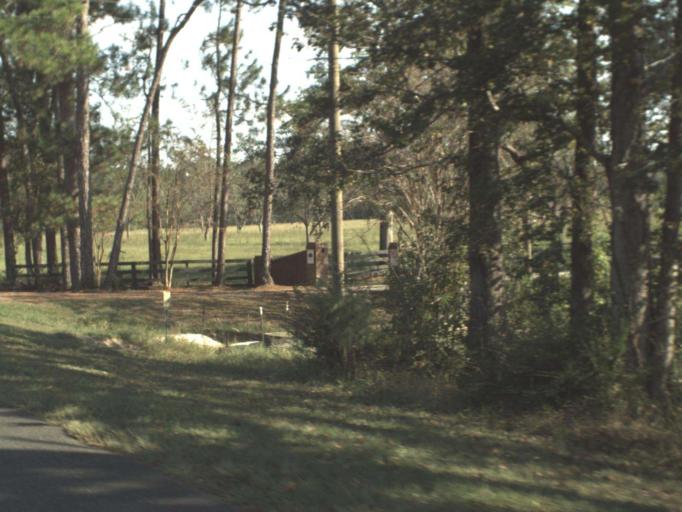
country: US
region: Florida
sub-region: Holmes County
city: Bonifay
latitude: 30.6552
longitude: -85.6991
